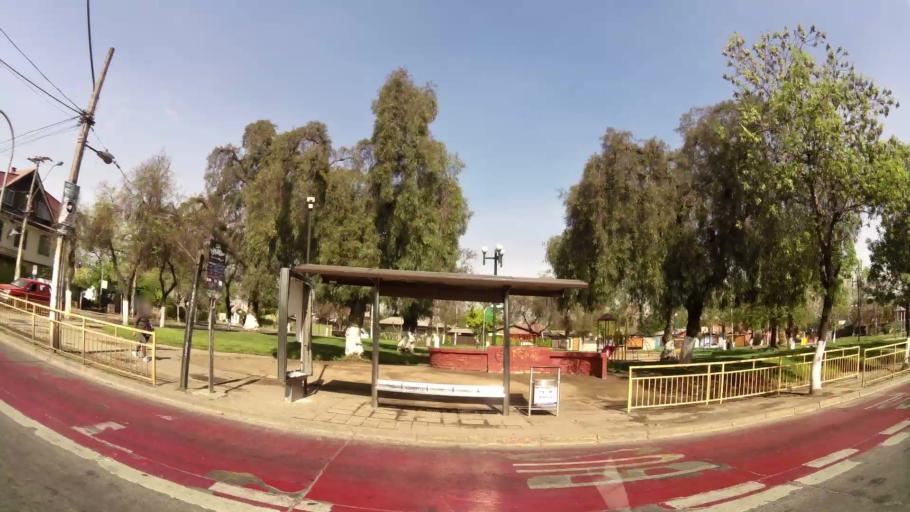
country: CL
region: Santiago Metropolitan
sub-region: Provincia de Santiago
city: Villa Presidente Frei, Nunoa, Santiago, Chile
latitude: -33.5008
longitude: -70.5952
